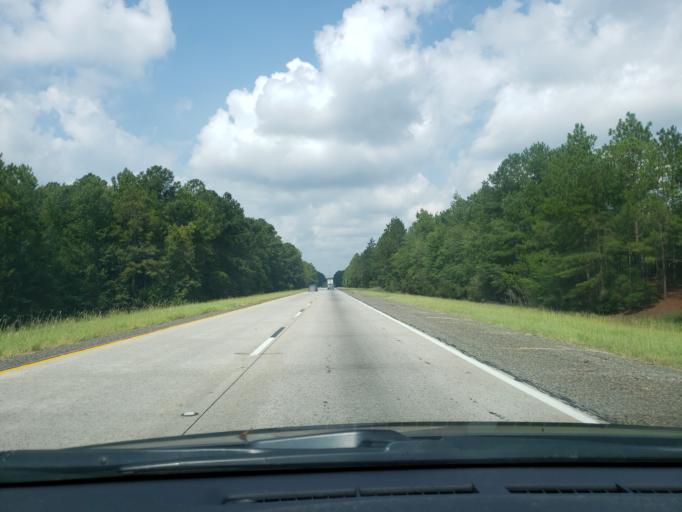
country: US
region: Georgia
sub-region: Treutlen County
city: Soperton
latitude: 32.4342
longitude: -82.6282
